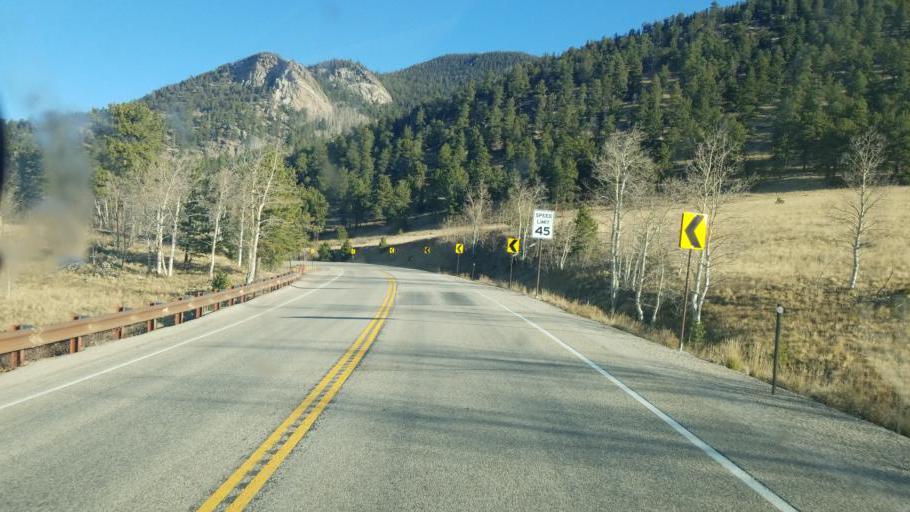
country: US
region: Colorado
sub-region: Teller County
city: Cripple Creek
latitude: 39.0402
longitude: -105.5265
